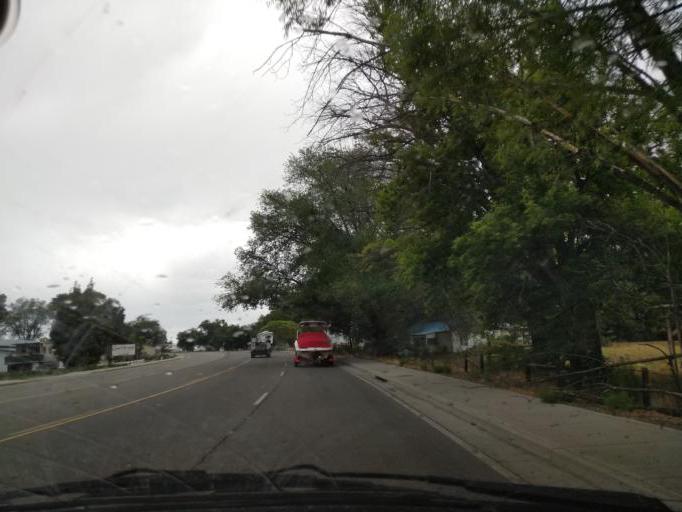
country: US
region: Colorado
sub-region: Delta County
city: Delta
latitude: 38.7621
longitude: -108.0719
